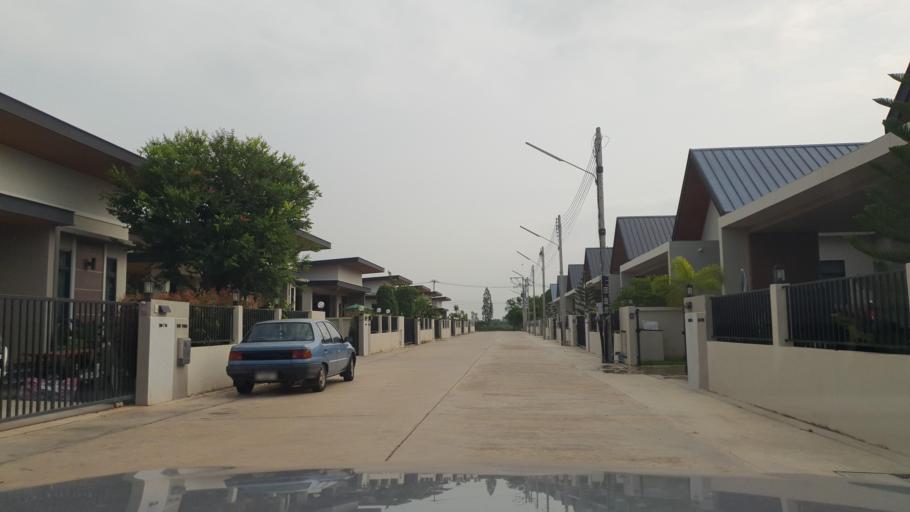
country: TH
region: Phitsanulok
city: Phitsanulok
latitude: 16.8129
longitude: 100.1874
